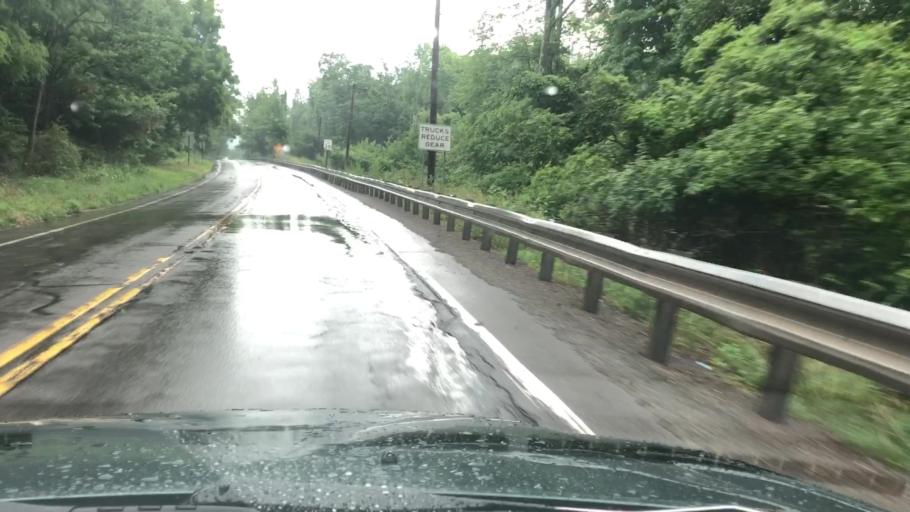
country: US
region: Pennsylvania
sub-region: Monroe County
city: Mountainhome
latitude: 41.1867
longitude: -75.2609
